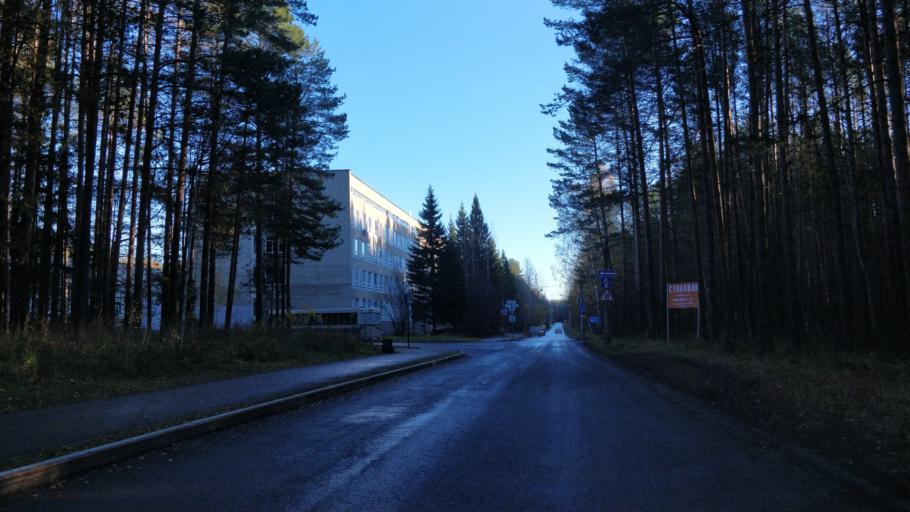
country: RU
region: Perm
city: Perm
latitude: 58.0534
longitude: 56.2301
